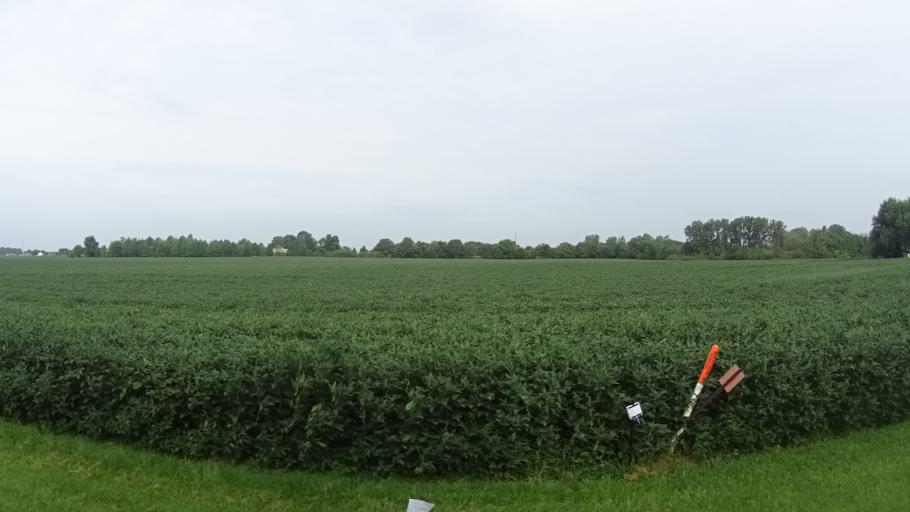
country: US
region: Indiana
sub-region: Madison County
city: Pendleton
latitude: 40.0198
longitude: -85.7389
